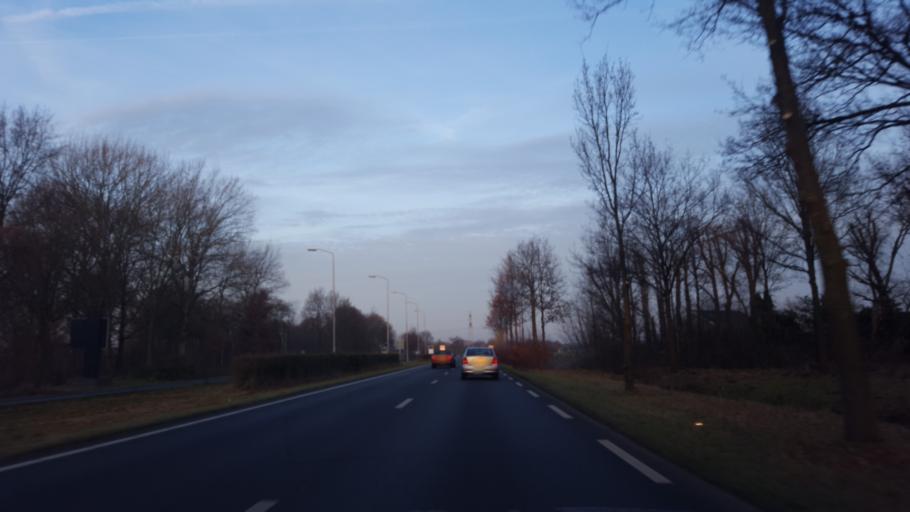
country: NL
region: Limburg
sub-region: Gemeente Weert
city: Weert
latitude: 51.2659
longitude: 5.6878
